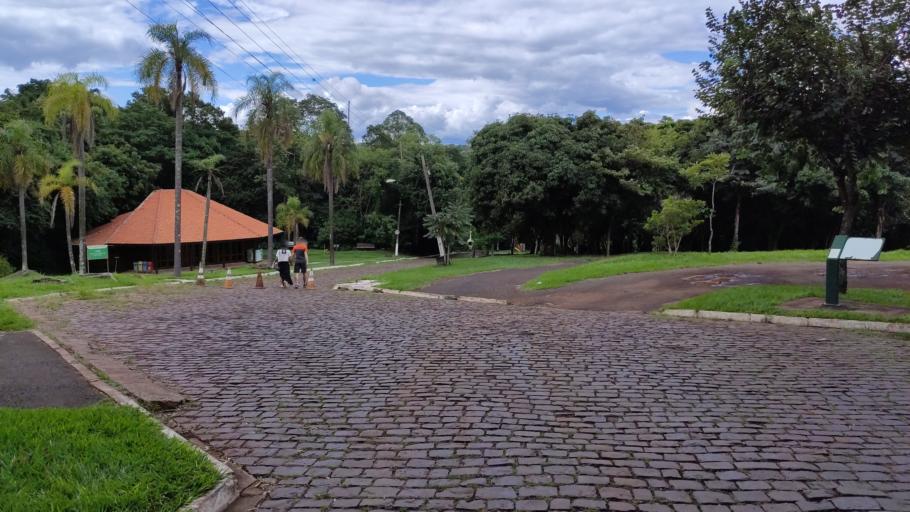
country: BR
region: Parana
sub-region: Londrina
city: Londrina
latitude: -23.3460
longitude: -51.1421
